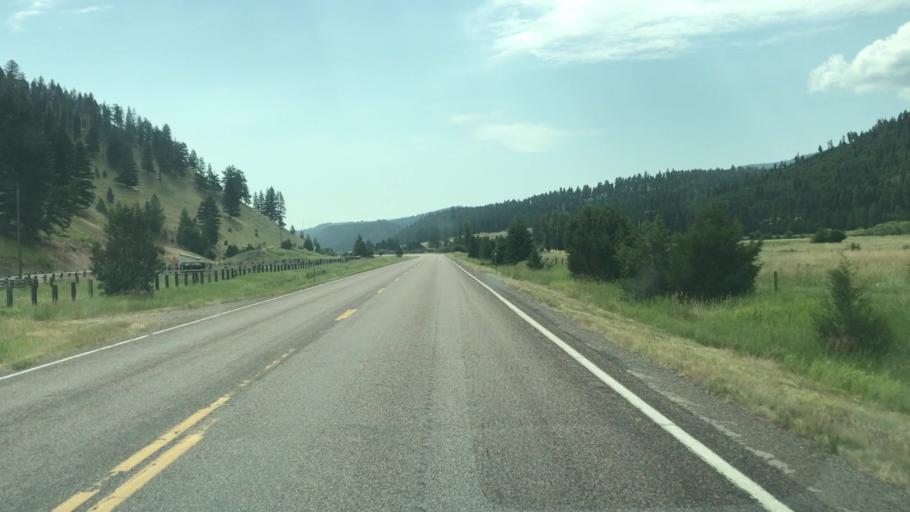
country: US
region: Montana
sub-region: Lewis and Clark County
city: Lincoln
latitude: 46.8225
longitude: -112.8636
